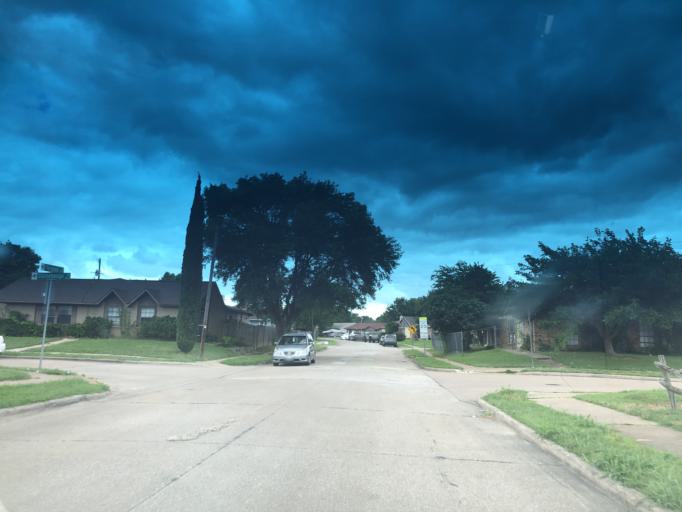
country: US
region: Texas
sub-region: Dallas County
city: Grand Prairie
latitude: 32.6988
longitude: -97.0073
